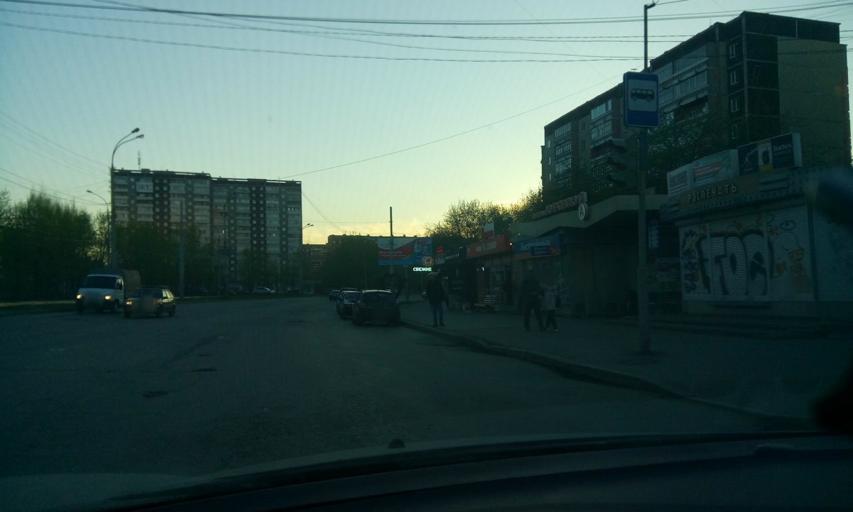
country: RU
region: Sverdlovsk
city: Yekaterinburg
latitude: 56.8352
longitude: 60.6847
